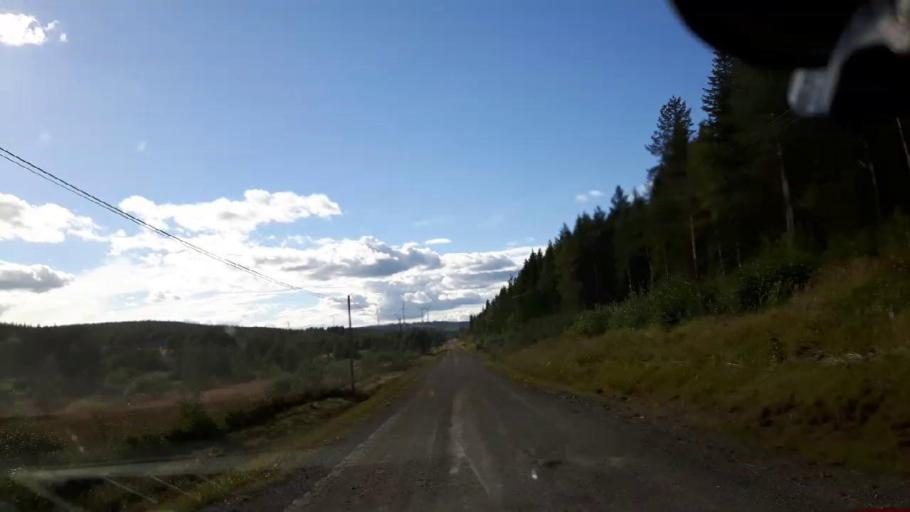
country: SE
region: Jaemtland
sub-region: Ragunda Kommun
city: Hammarstrand
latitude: 63.4881
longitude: 16.0849
